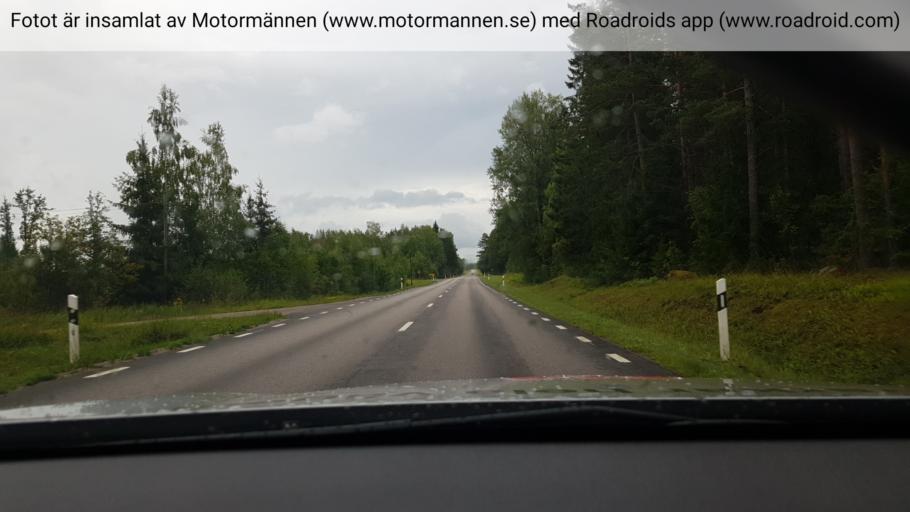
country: SE
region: Uppsala
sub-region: Tierps Kommun
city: Karlholmsbruk
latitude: 60.5428
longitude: 17.5452
